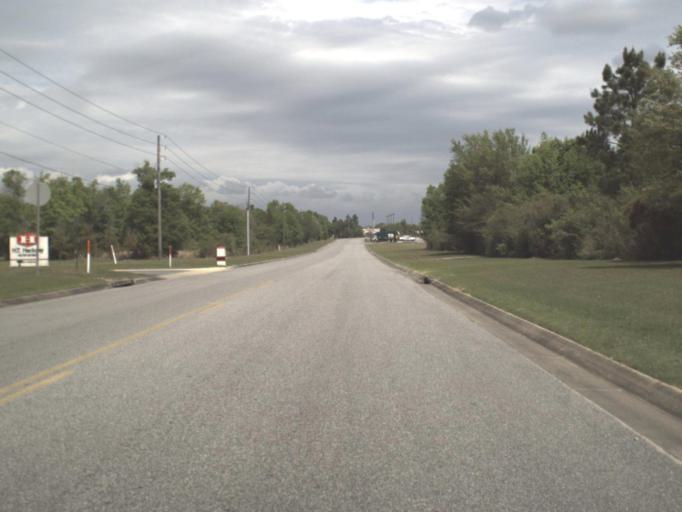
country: US
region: Florida
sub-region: Santa Rosa County
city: East Milton
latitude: 30.6362
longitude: -86.9727
